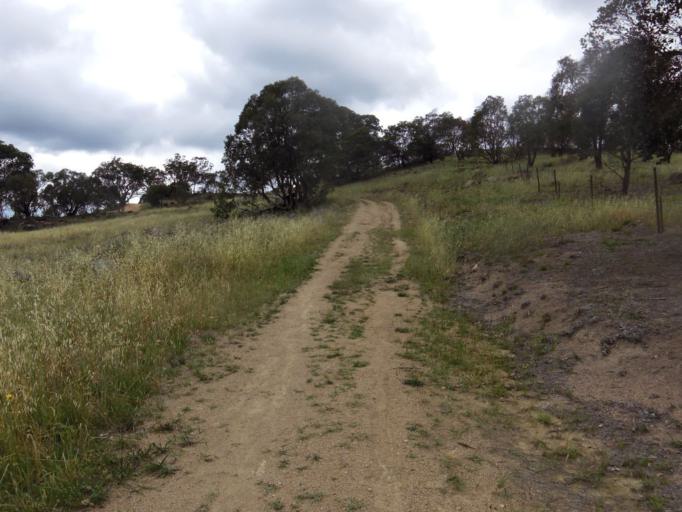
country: AU
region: Australian Capital Territory
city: Macquarie
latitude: -35.3518
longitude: 149.0223
